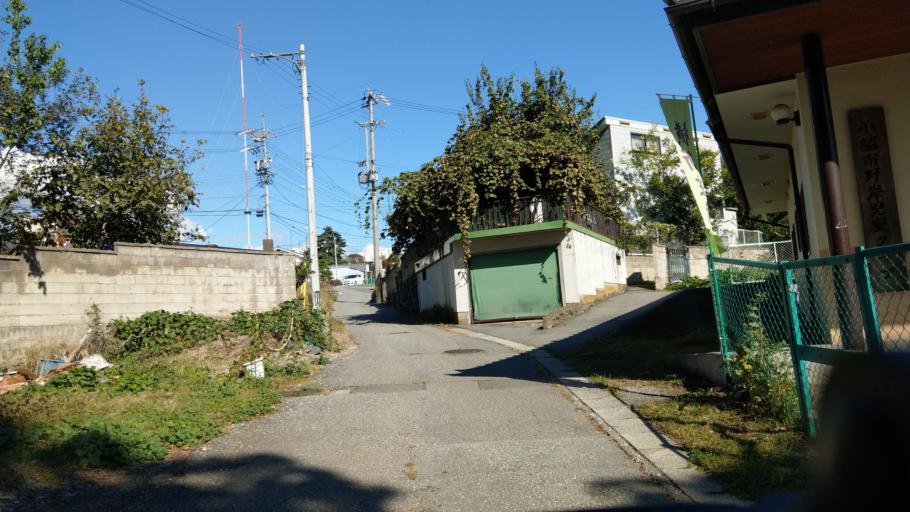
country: JP
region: Nagano
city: Komoro
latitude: 36.3259
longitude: 138.4323
